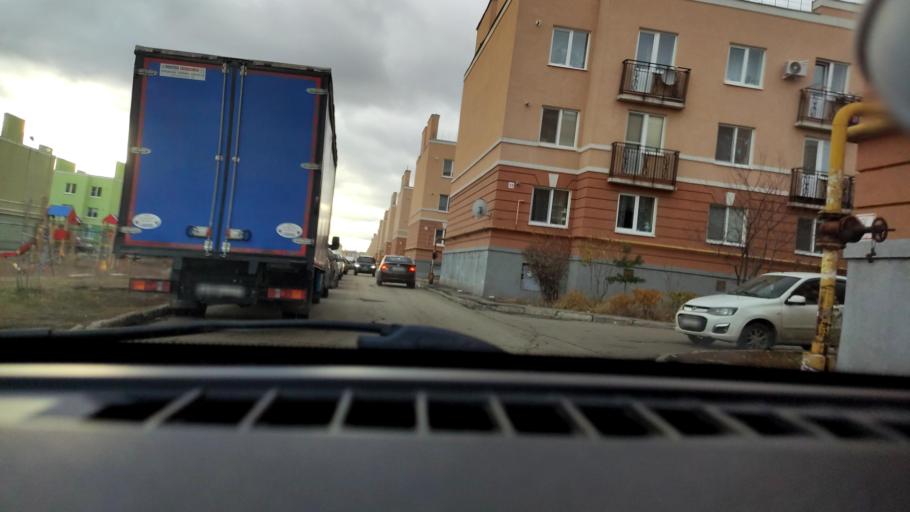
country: RU
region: Samara
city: Petra-Dubrava
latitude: 53.3198
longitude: 50.3124
